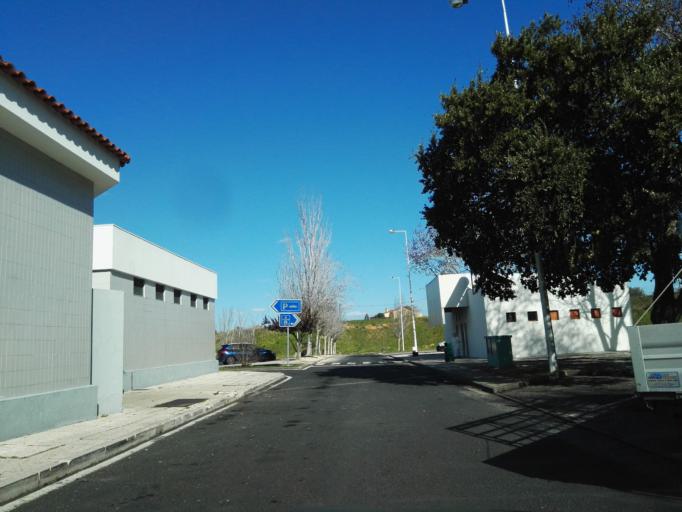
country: PT
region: Lisbon
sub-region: Azambuja
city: Aveiras de Cima
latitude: 39.1220
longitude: -8.9080
